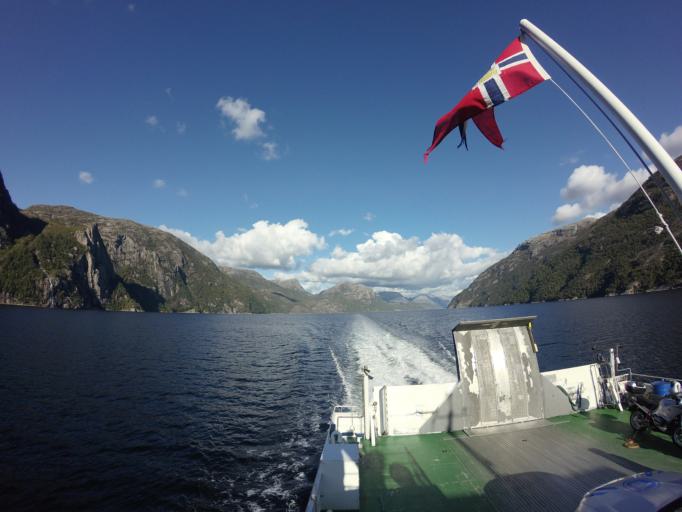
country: NO
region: Rogaland
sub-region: Forsand
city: Forsand
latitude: 58.9904
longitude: 6.2309
